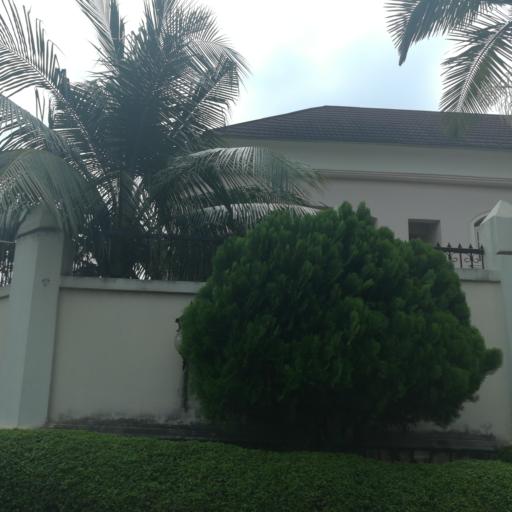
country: NG
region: Lagos
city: Ojota
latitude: 6.5736
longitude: 3.3917
